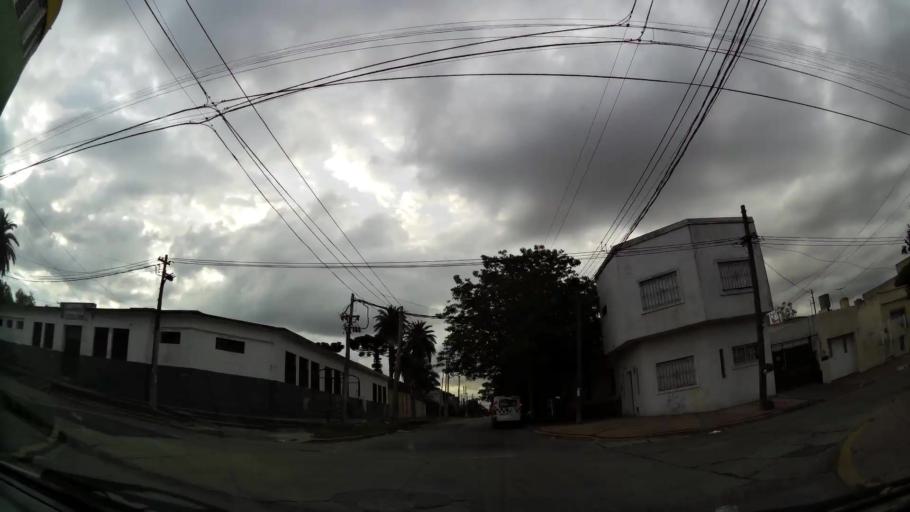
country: AR
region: Buenos Aires
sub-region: Partido de Quilmes
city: Quilmes
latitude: -34.7380
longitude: -58.2451
